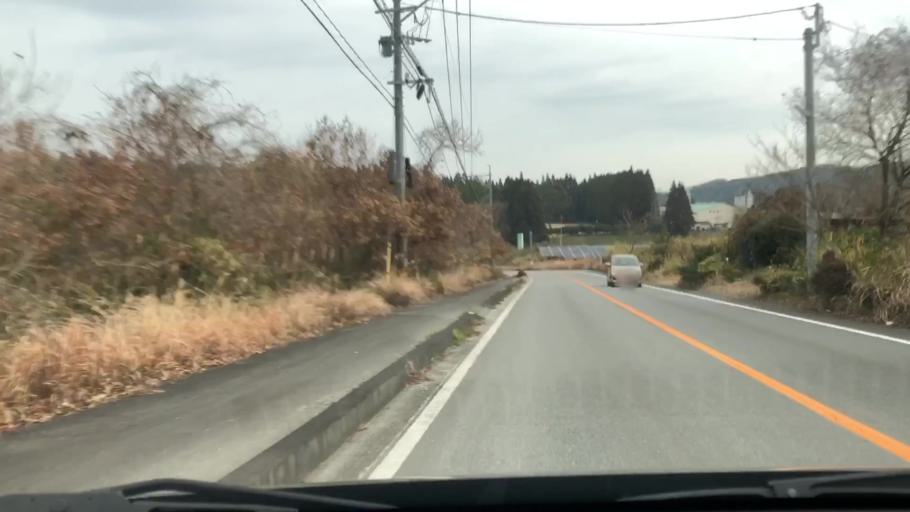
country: JP
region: Oita
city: Usuki
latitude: 33.0066
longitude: 131.6306
